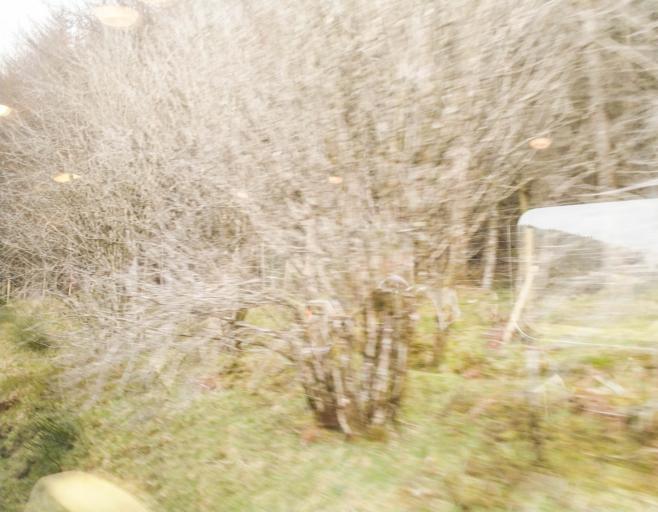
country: GB
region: Scotland
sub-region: Argyll and Bute
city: Garelochhead
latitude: 56.4420
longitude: -4.7077
